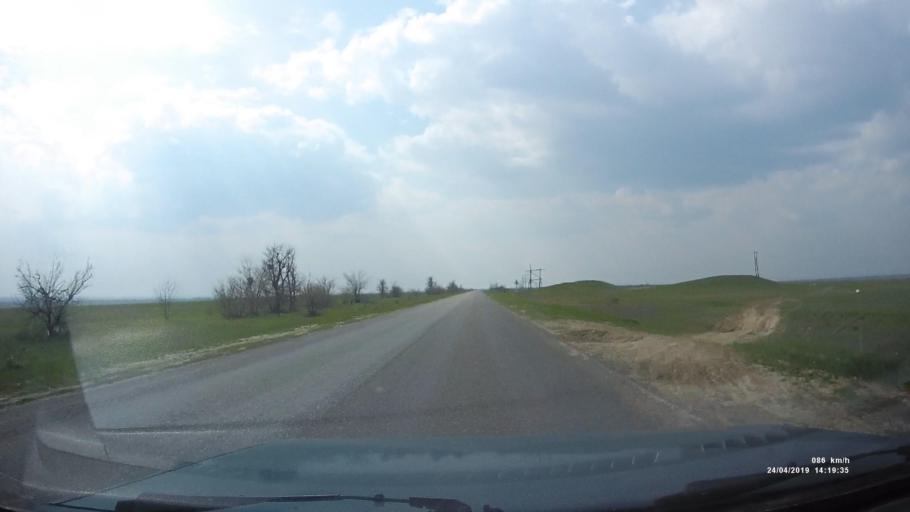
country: RU
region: Kalmykiya
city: Arshan'
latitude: 46.3059
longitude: 44.1731
